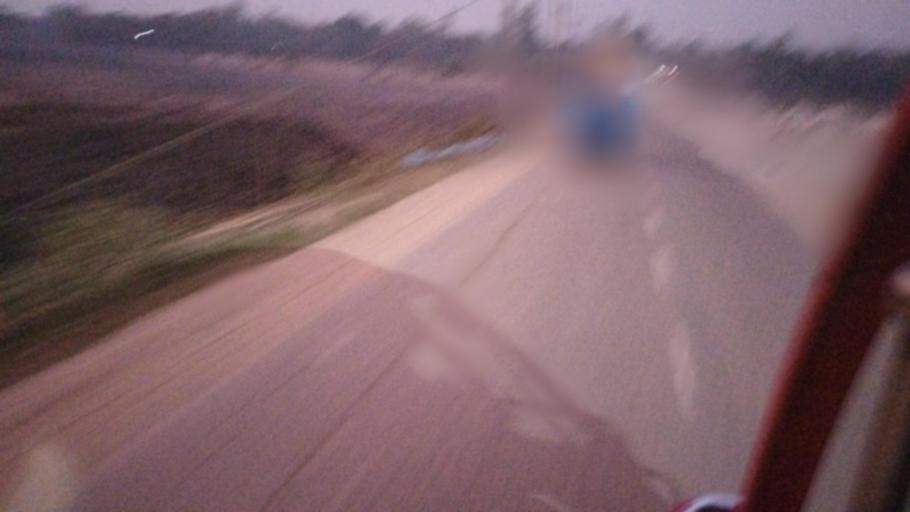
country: BD
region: Dhaka
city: Sakhipur
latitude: 24.3941
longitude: 90.3332
